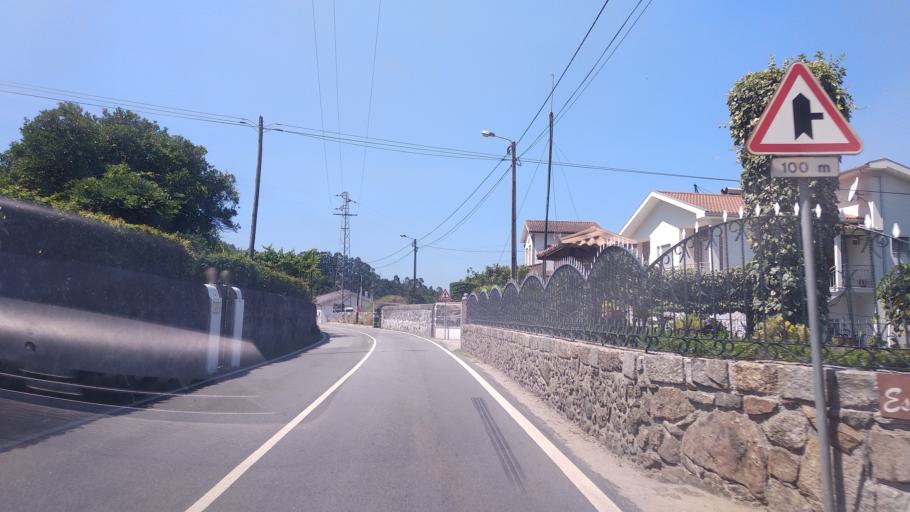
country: PT
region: Braga
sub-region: Braga
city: Adaufe
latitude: 41.5808
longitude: -8.4072
